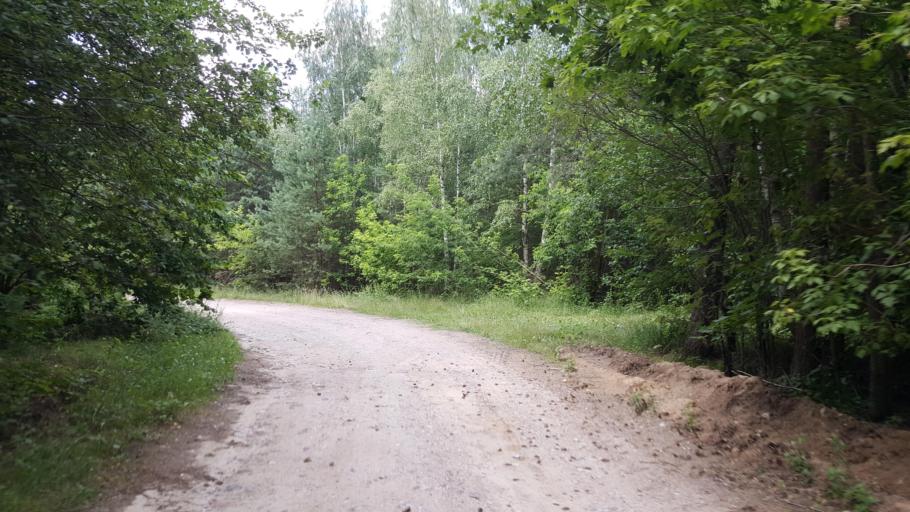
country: BY
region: Brest
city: Kamyanyets
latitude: 52.3445
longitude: 23.9159
